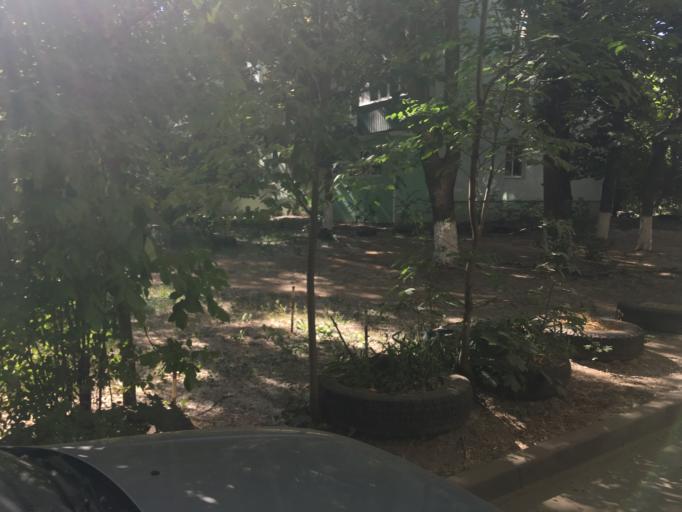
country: RU
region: Rostov
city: Rostov-na-Donu
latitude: 47.2095
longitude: 39.6257
